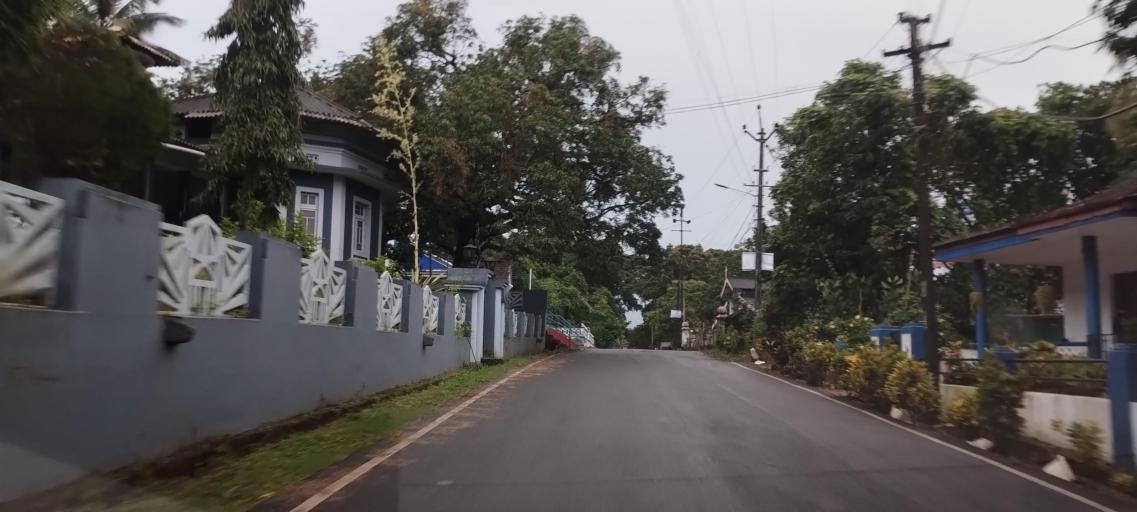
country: IN
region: Goa
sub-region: North Goa
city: Jua
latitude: 15.5252
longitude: 73.9027
